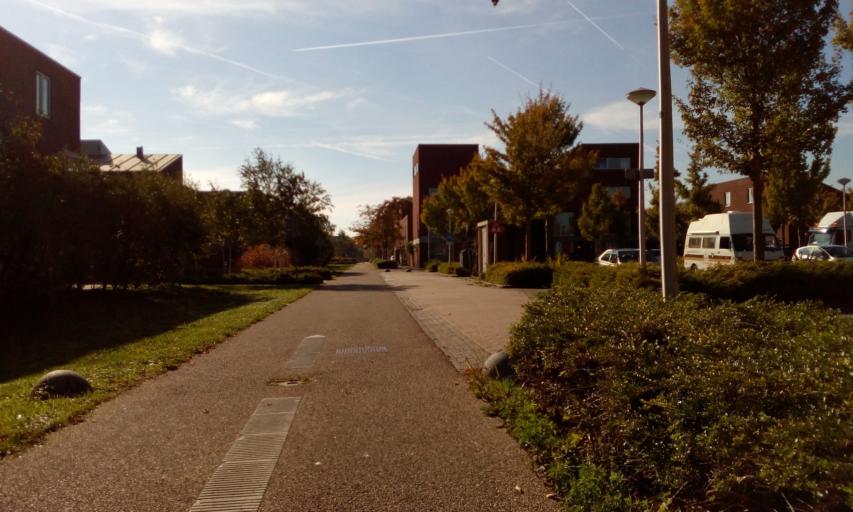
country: NL
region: Utrecht
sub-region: Stichtse Vecht
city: Spechtenkamp
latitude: 52.0821
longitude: 5.0232
